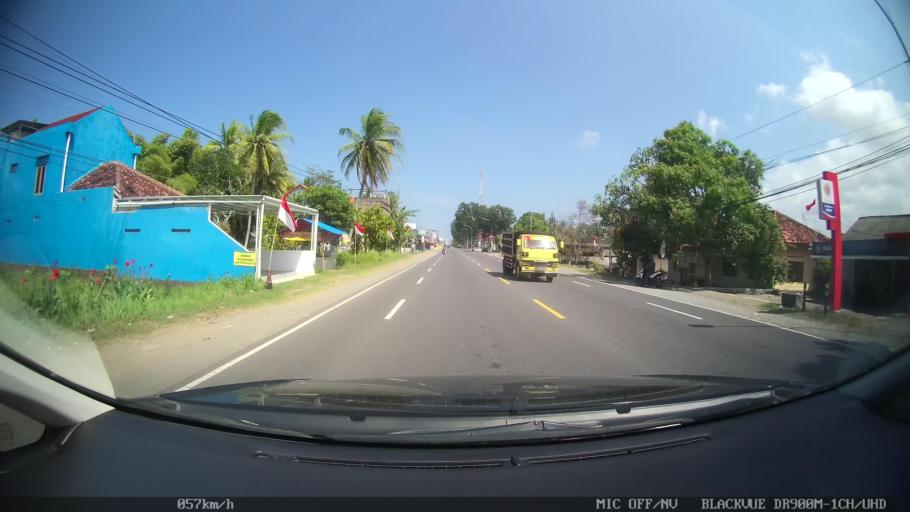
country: ID
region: Daerah Istimewa Yogyakarta
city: Srandakan
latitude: -7.8872
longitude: 110.0824
